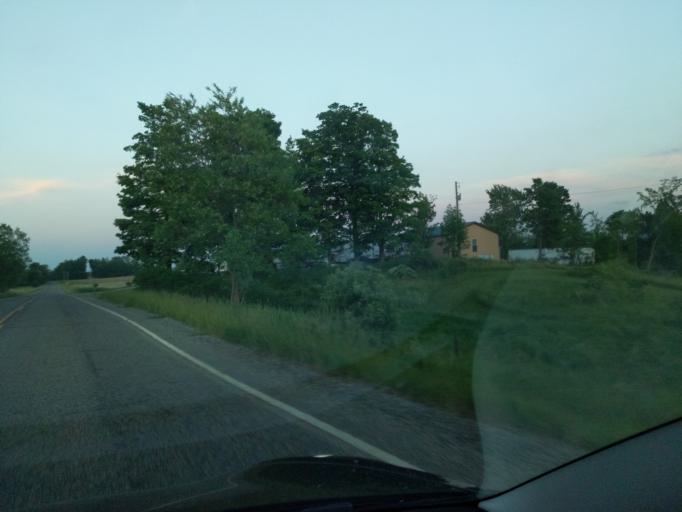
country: US
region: Michigan
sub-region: Barry County
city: Nashville
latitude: 42.5383
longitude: -85.0396
